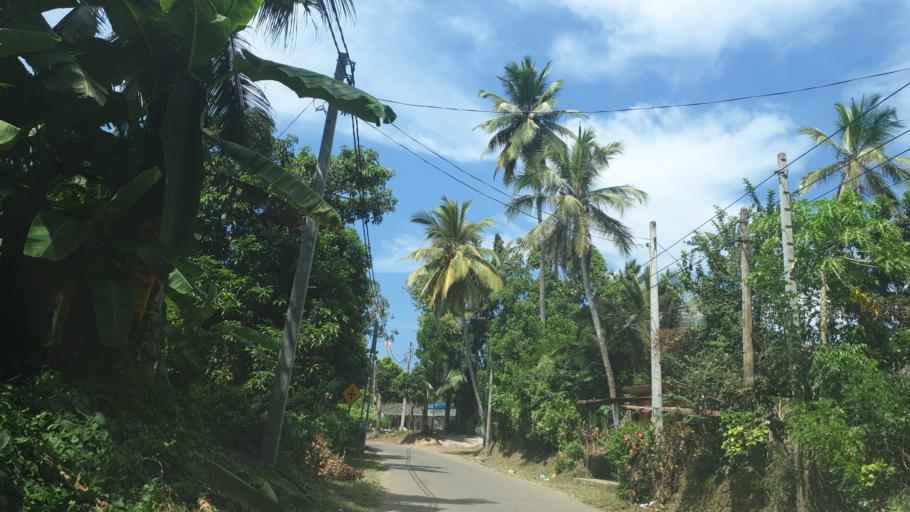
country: LK
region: Southern
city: Matara
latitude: 5.9748
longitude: 80.6580
